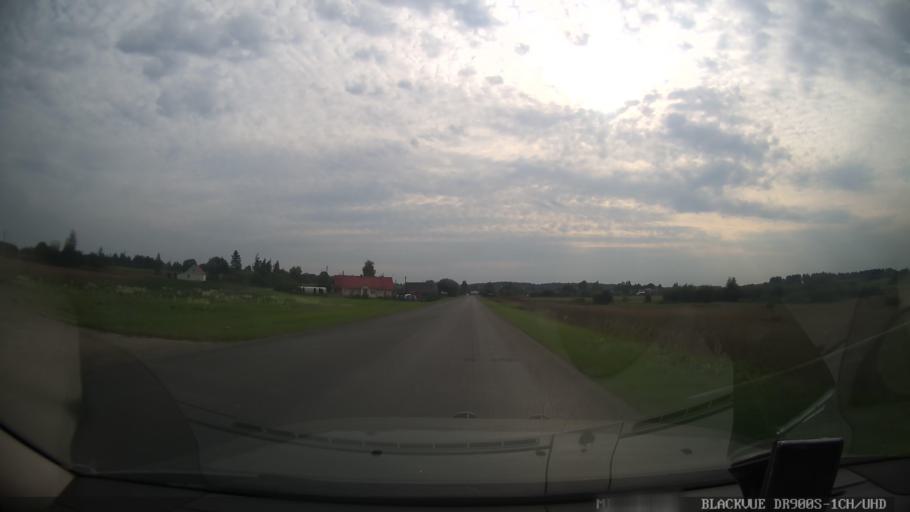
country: LT
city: Skaidiskes
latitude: 54.5475
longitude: 25.6532
